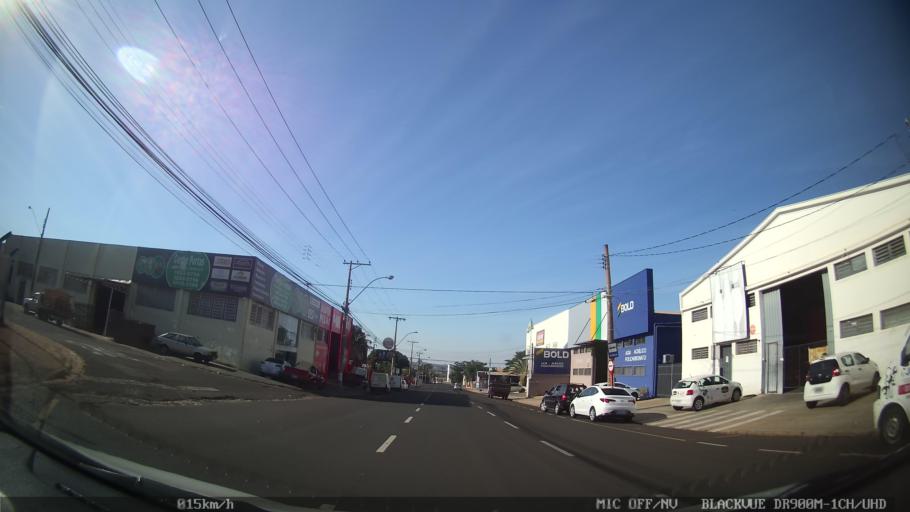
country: BR
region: Sao Paulo
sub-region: Sao Jose Do Rio Preto
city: Sao Jose do Rio Preto
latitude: -20.7884
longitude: -49.3566
